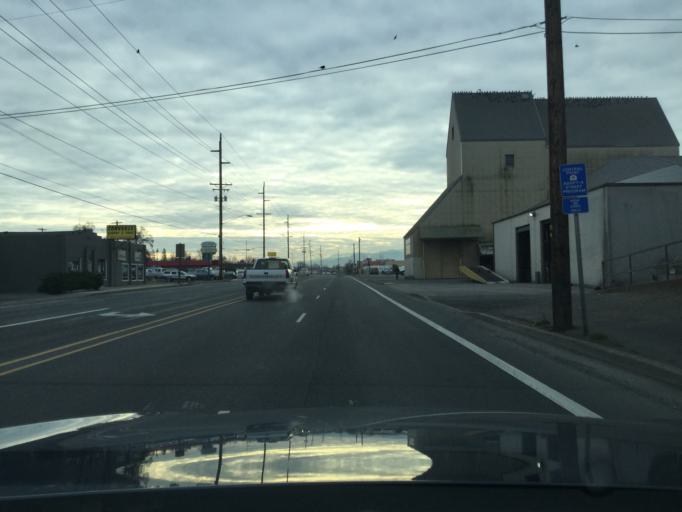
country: US
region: Oregon
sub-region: Jackson County
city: Central Point
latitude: 42.3735
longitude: -122.9177
